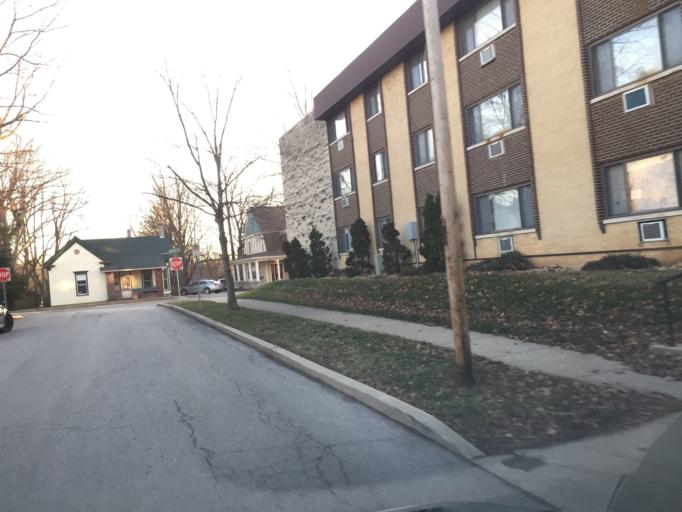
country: US
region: Indiana
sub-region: Monroe County
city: Bloomington
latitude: 39.1619
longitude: -86.5284
